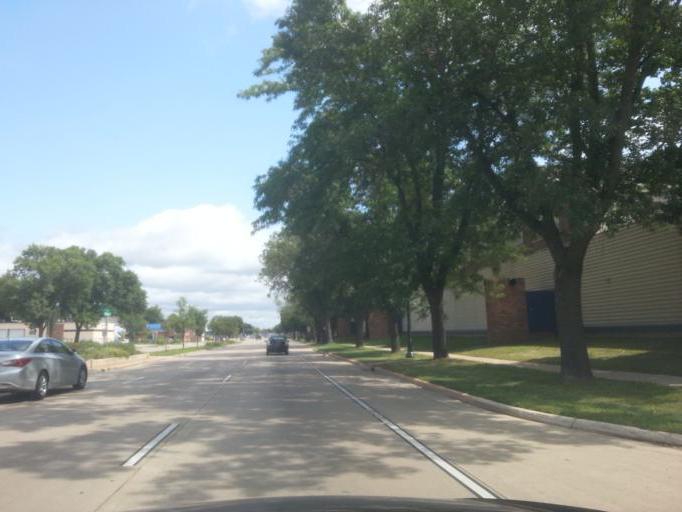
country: US
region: Wisconsin
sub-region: Dane County
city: Maple Bluff
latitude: 43.0857
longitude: -89.3684
